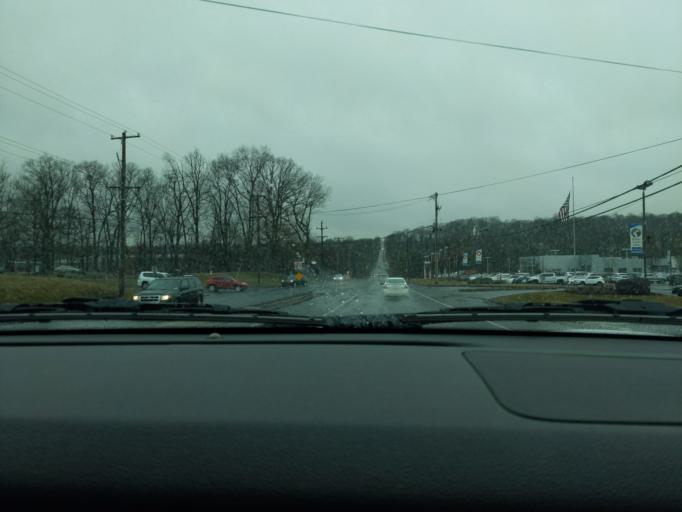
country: US
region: Pennsylvania
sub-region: Bucks County
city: Doylestown
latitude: 40.3328
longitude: -75.1370
